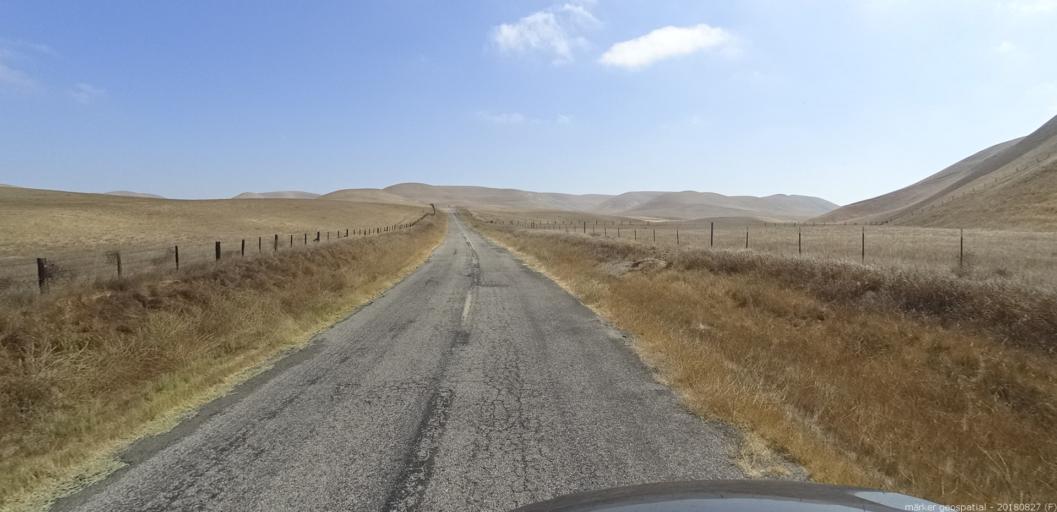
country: US
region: California
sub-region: Monterey County
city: King City
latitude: 36.2316
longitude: -121.0484
